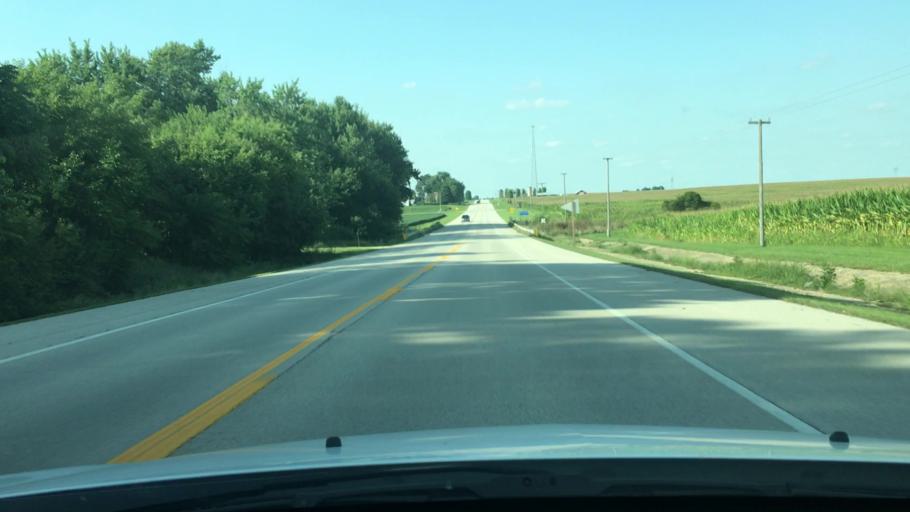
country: US
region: Illinois
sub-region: DeKalb County
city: Waterman
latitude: 41.7870
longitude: -88.7542
